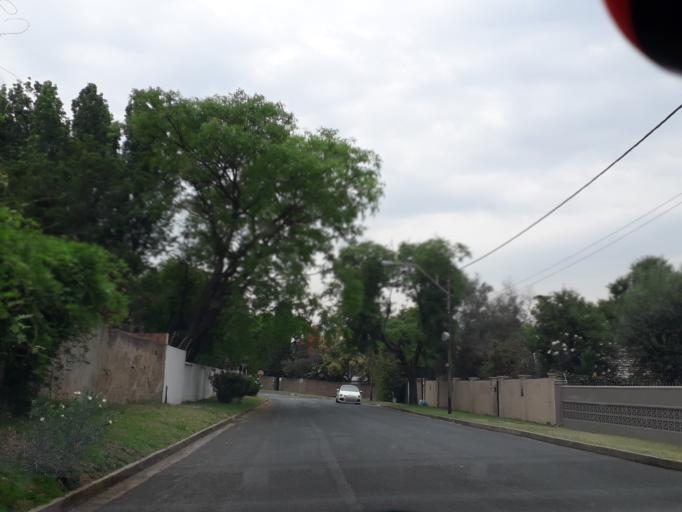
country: ZA
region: Gauteng
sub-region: City of Johannesburg Metropolitan Municipality
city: Johannesburg
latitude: -26.1289
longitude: 28.0783
